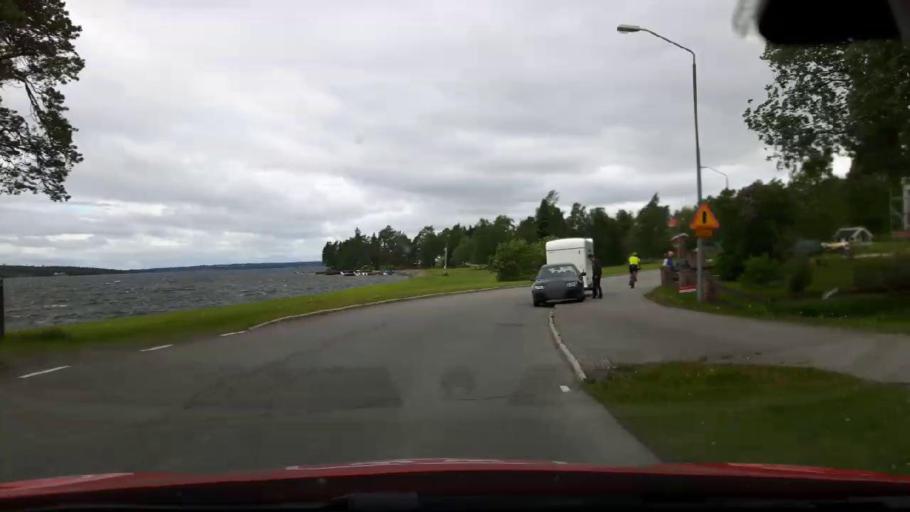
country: SE
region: Jaemtland
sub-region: OEstersunds Kommun
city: Ostersund
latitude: 63.2002
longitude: 14.6368
